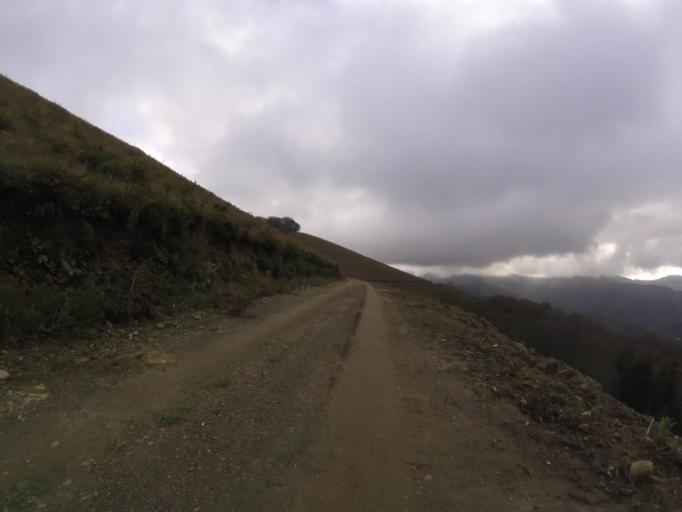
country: ES
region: Navarre
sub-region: Provincia de Navarra
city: Goizueta
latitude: 43.1991
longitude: -1.8257
